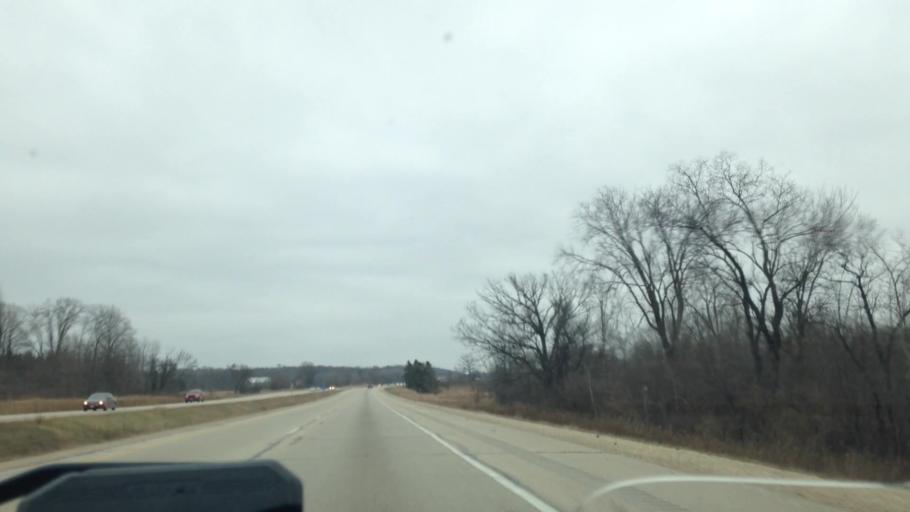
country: US
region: Wisconsin
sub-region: Washington County
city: Slinger
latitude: 43.3925
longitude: -88.3150
